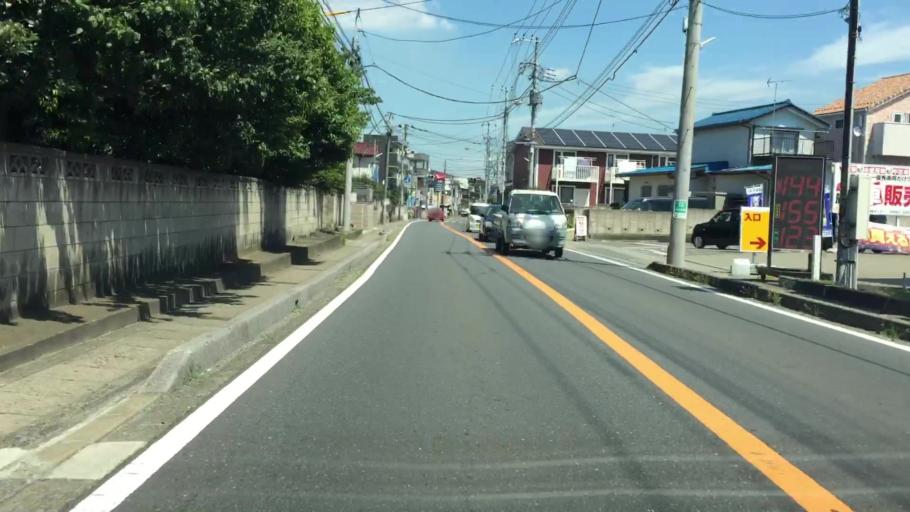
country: JP
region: Chiba
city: Funabashi
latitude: 35.7289
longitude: 139.9633
